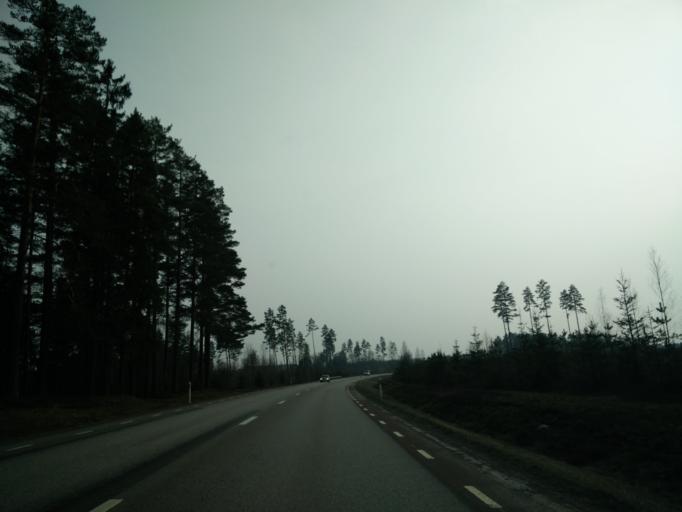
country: SE
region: Vaermland
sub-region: Forshaga Kommun
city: Forshaga
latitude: 59.5003
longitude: 13.4335
